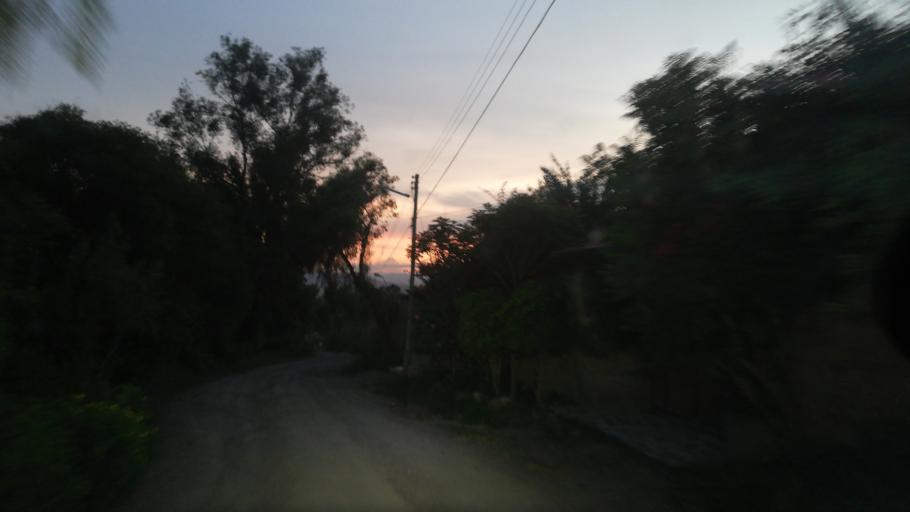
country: BO
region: Cochabamba
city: Cochabamba
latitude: -17.3322
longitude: -66.2078
